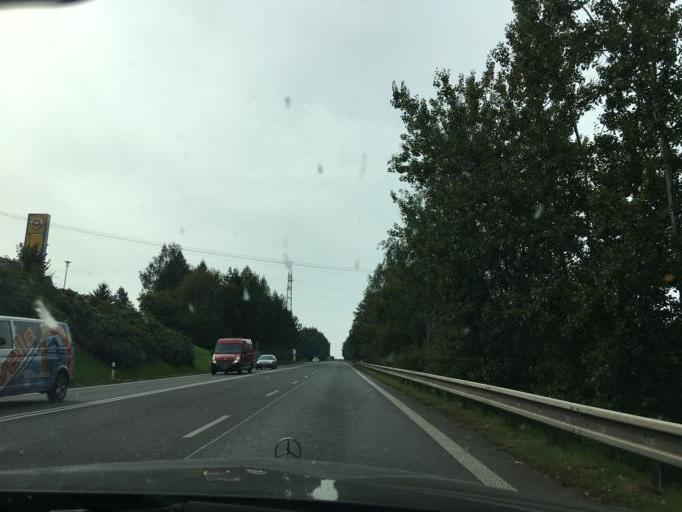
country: CZ
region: Kralovehradecky
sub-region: Okres Nachod
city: Nachod
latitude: 50.4076
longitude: 16.1403
